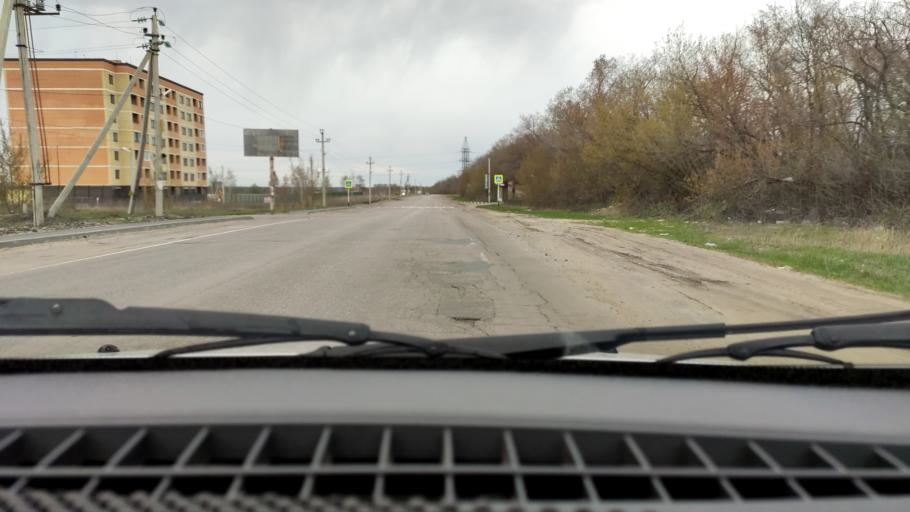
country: RU
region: Voronezj
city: Novaya Usman'
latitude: 51.6265
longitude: 39.3343
